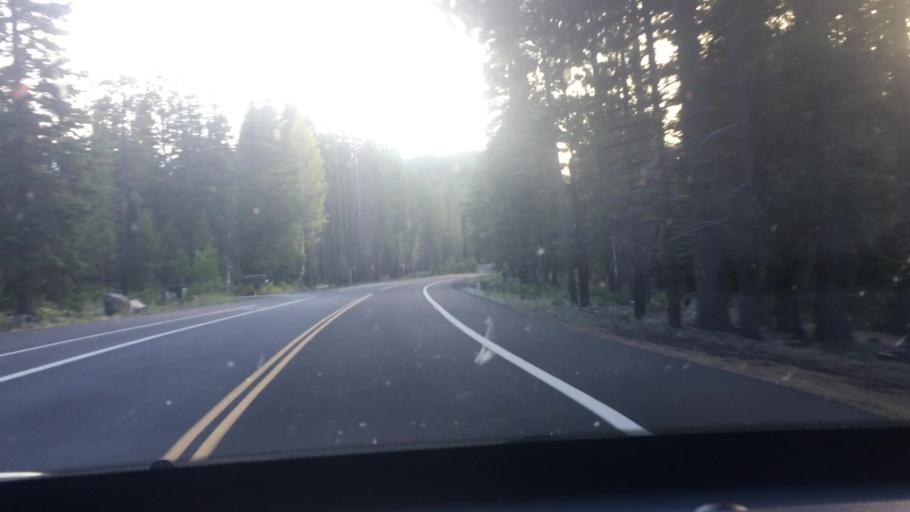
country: US
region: Oregon
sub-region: Deschutes County
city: Deschutes River Woods
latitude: 44.0314
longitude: -121.5167
